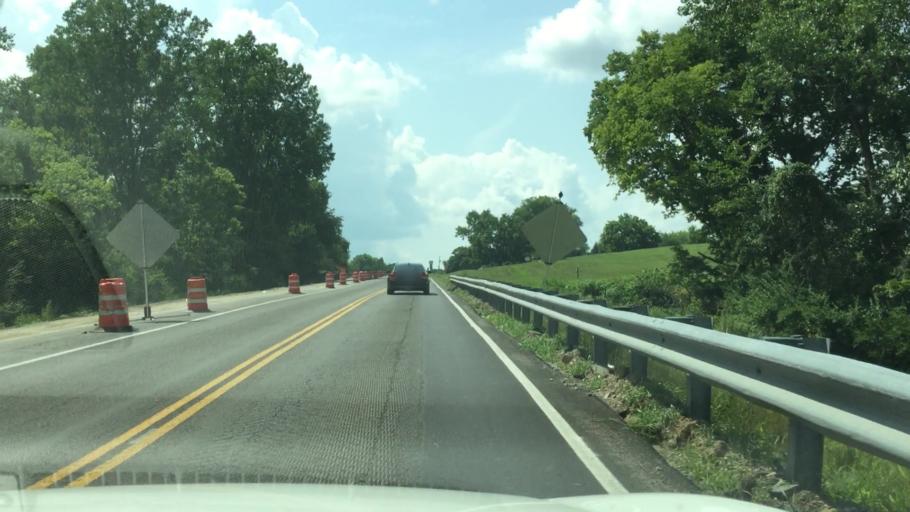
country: US
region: Ohio
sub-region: Clark County
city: Northridge
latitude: 39.9506
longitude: -83.7611
